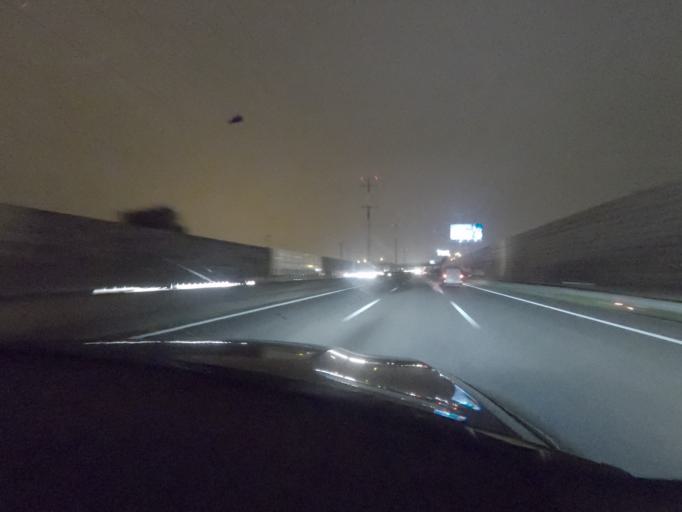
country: PT
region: Lisbon
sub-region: Loures
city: Santa Iria da Azoia
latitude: 38.8373
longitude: -9.0956
